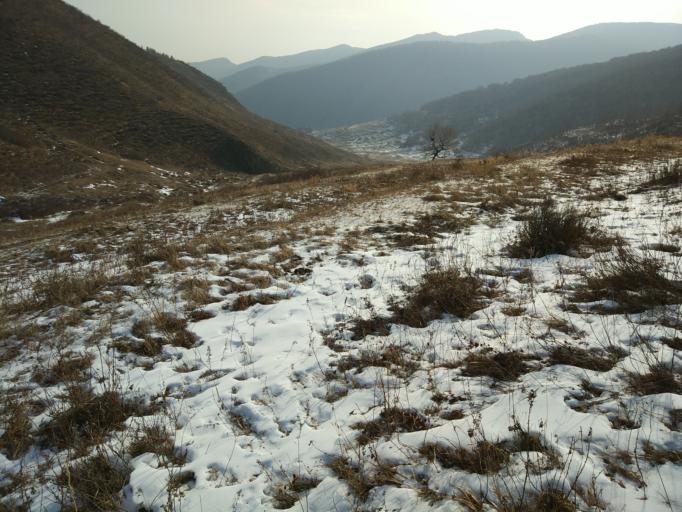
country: CN
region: Hebei
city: Xiwanzi
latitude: 40.8581
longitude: 115.4554
